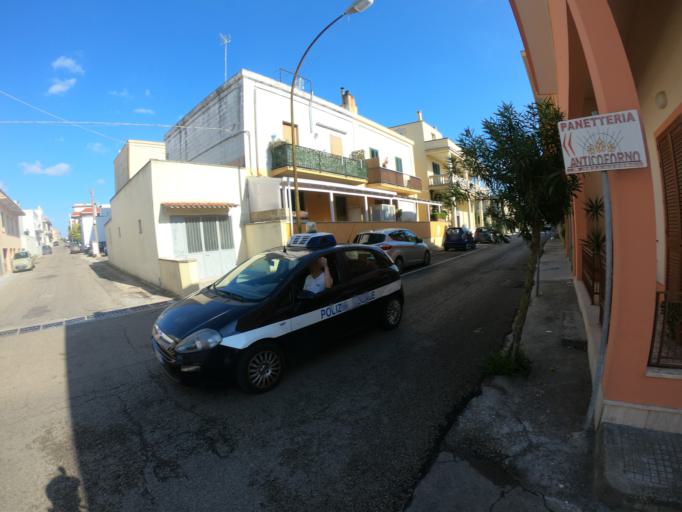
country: IT
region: Apulia
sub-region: Provincia di Lecce
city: Supersano
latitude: 40.0141
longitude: 18.2413
